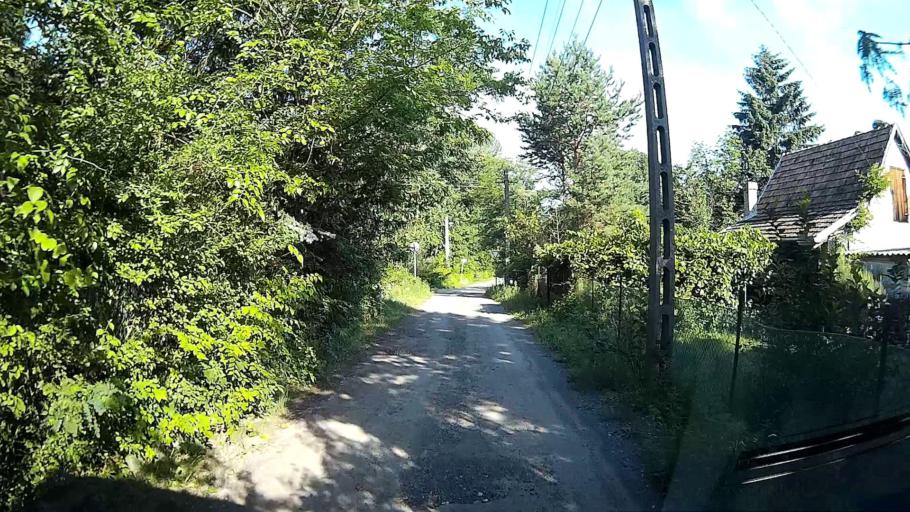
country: HU
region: Pest
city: God
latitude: 47.6802
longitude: 19.1130
